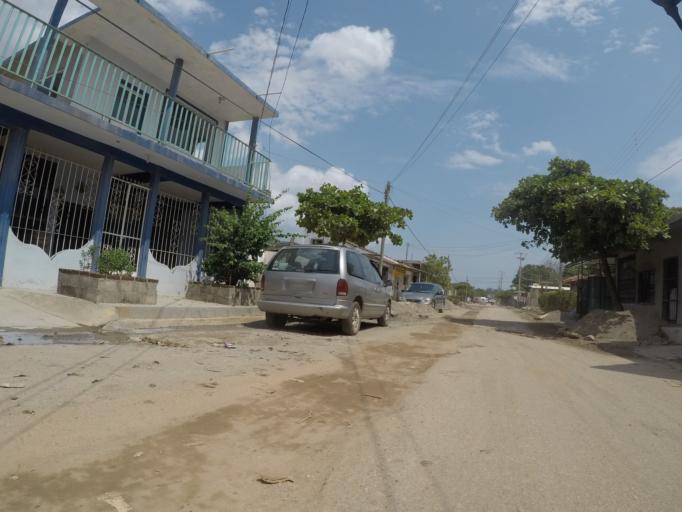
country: MX
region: Oaxaca
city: Union Hidalgo
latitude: 16.4687
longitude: -94.8285
